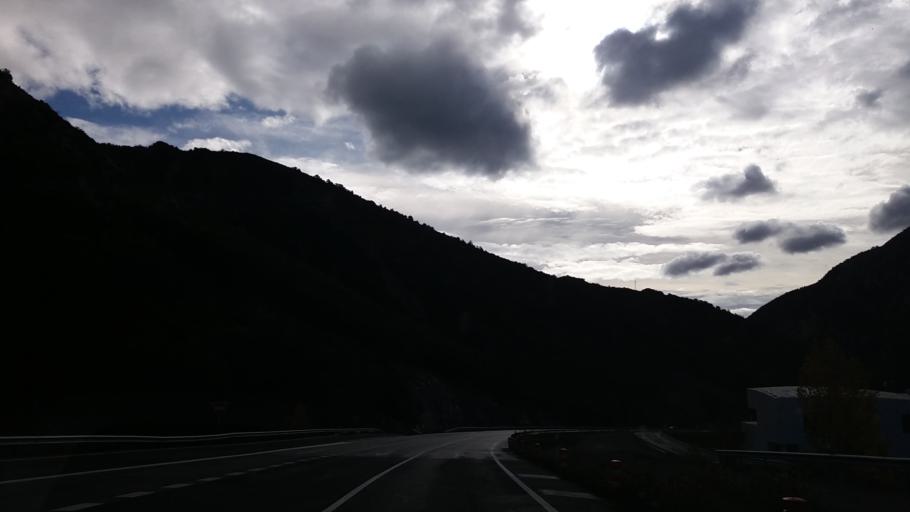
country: ES
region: Aragon
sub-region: Provincia de Huesca
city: Arguis
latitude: 42.3099
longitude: -0.4244
